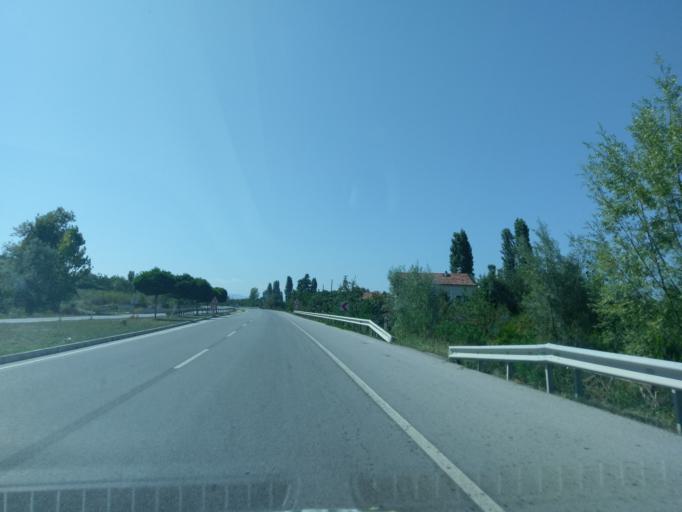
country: TR
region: Samsun
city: Alacam
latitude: 41.6125
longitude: 35.7105
